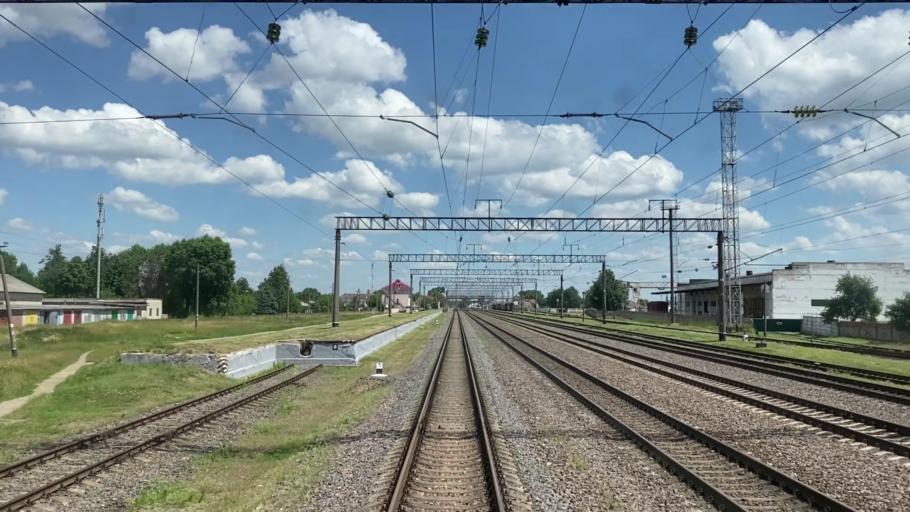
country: BY
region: Brest
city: Ivatsevichy
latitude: 52.7063
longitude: 25.3383
